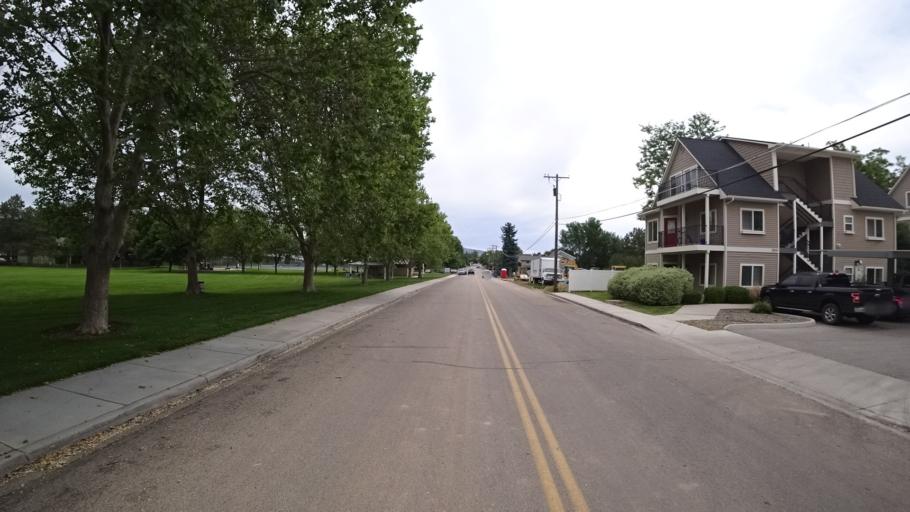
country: US
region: Idaho
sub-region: Ada County
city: Boise
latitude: 43.5772
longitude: -116.2178
